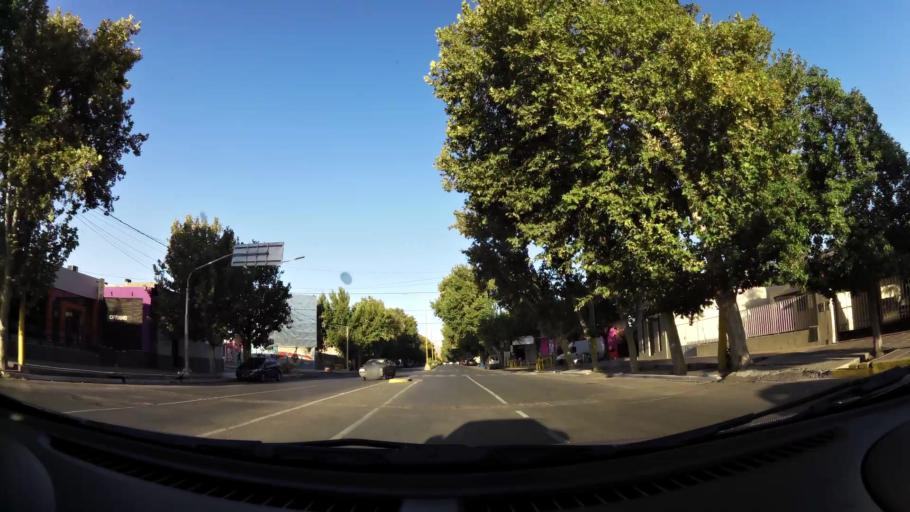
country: AR
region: San Juan
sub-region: Departamento de Santa Lucia
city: Santa Lucia
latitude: -31.5414
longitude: -68.5029
